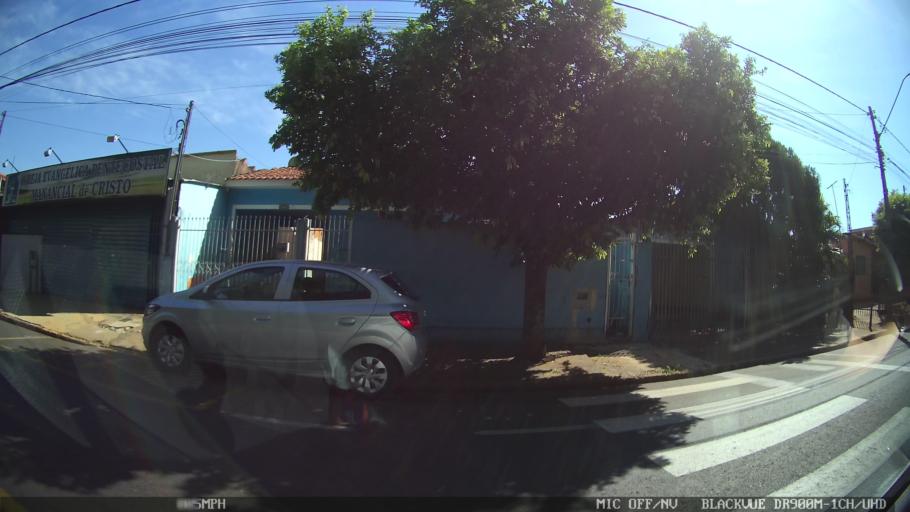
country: BR
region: Sao Paulo
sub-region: Sao Jose Do Rio Preto
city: Sao Jose do Rio Preto
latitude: -20.7737
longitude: -49.4181
